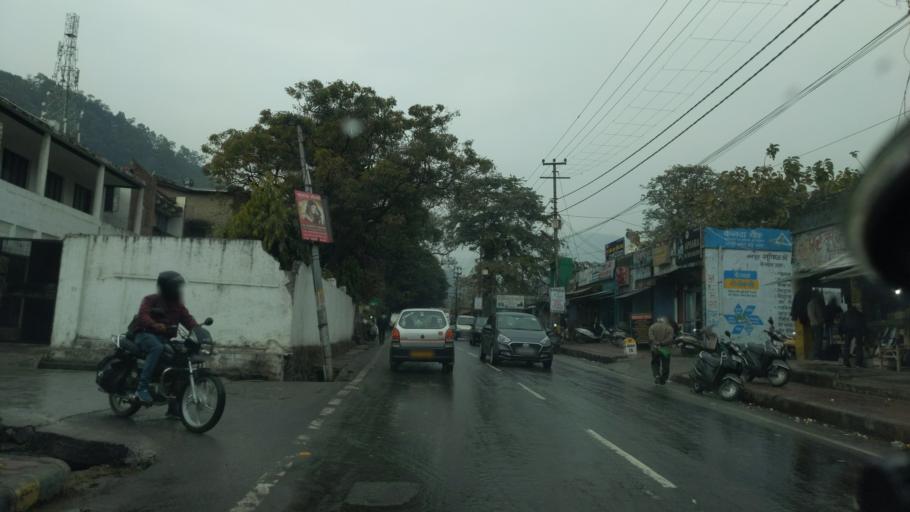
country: IN
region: Uttarakhand
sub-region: Naini Tal
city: Haldwani
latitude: 29.2682
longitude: 79.5444
